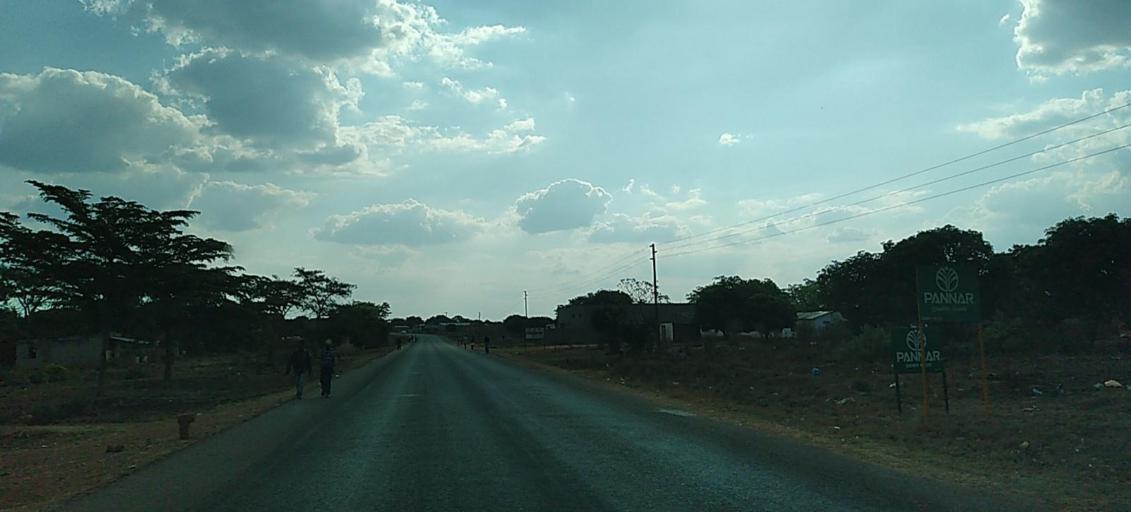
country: ZM
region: Copperbelt
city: Luanshya
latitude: -13.3628
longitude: 28.4111
